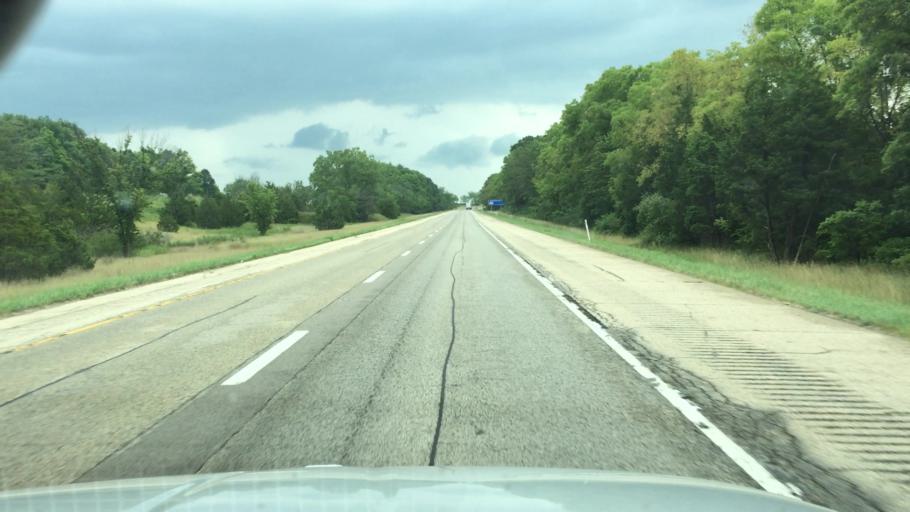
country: US
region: Illinois
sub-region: Peoria County
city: Hanna City
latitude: 40.7894
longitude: -89.7884
